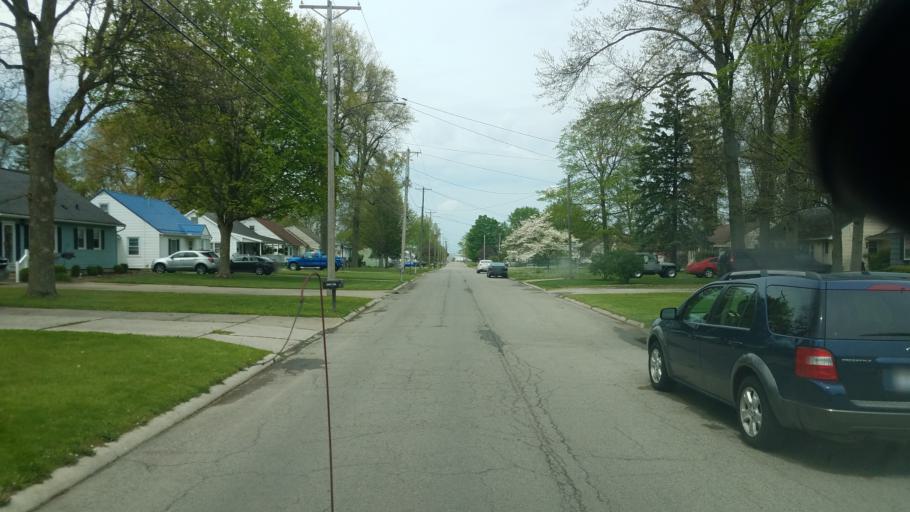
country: US
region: Ohio
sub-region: Richland County
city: Shelby
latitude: 40.8911
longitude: -82.6663
